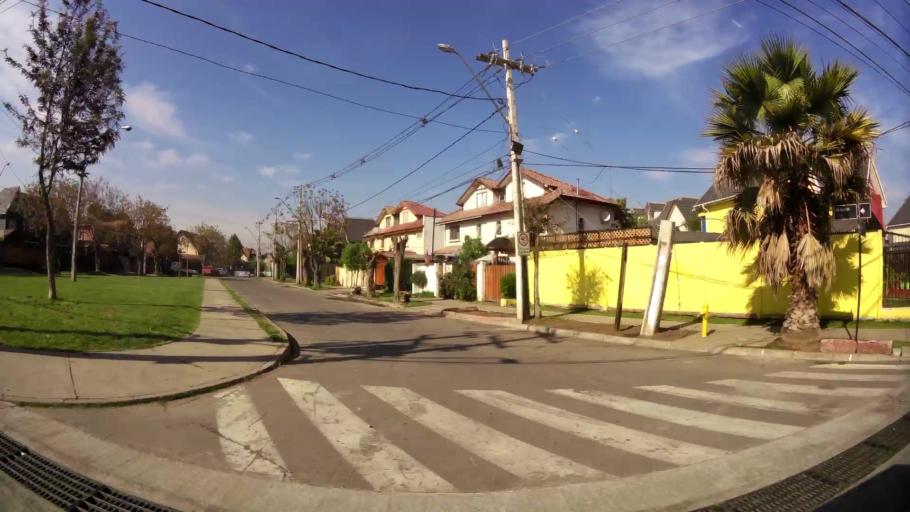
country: CL
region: Santiago Metropolitan
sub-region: Provincia de Santiago
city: Lo Prado
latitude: -33.4494
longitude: -70.7650
